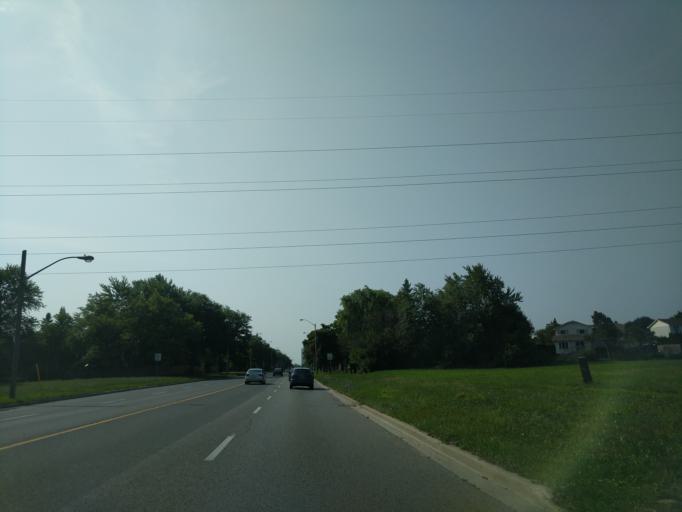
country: CA
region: Ontario
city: Scarborough
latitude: 43.8168
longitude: -79.2715
